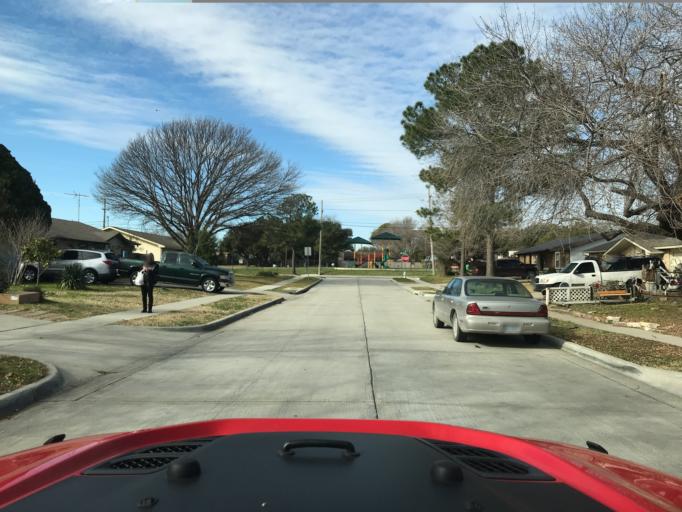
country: US
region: Texas
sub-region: Denton County
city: Lewisville
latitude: 33.0383
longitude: -97.0267
